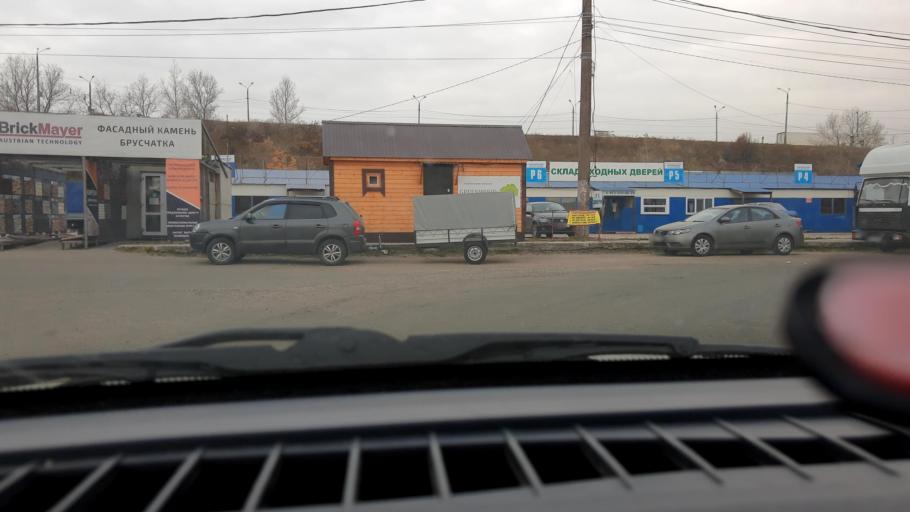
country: RU
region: Nizjnij Novgorod
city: Nizhniy Novgorod
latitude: 56.2548
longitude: 43.9423
